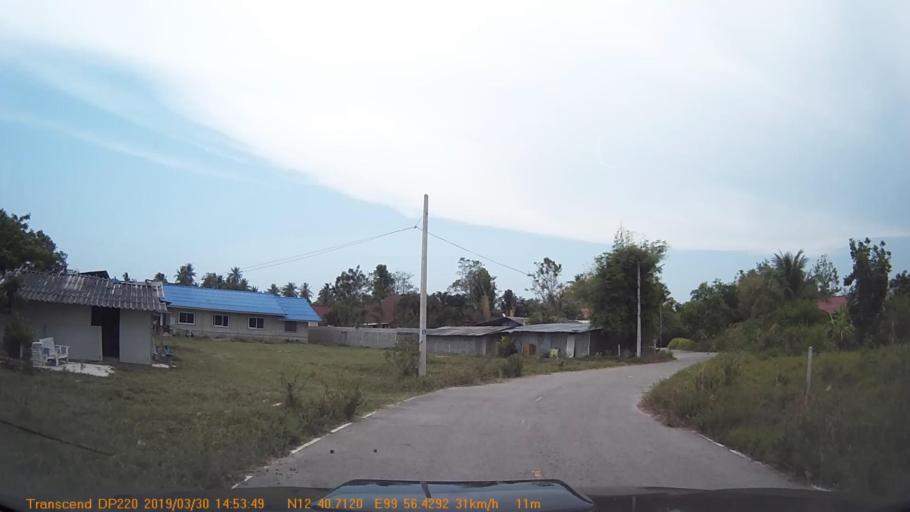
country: TH
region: Prachuap Khiri Khan
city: Hua Hin
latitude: 12.6784
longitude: 99.9406
